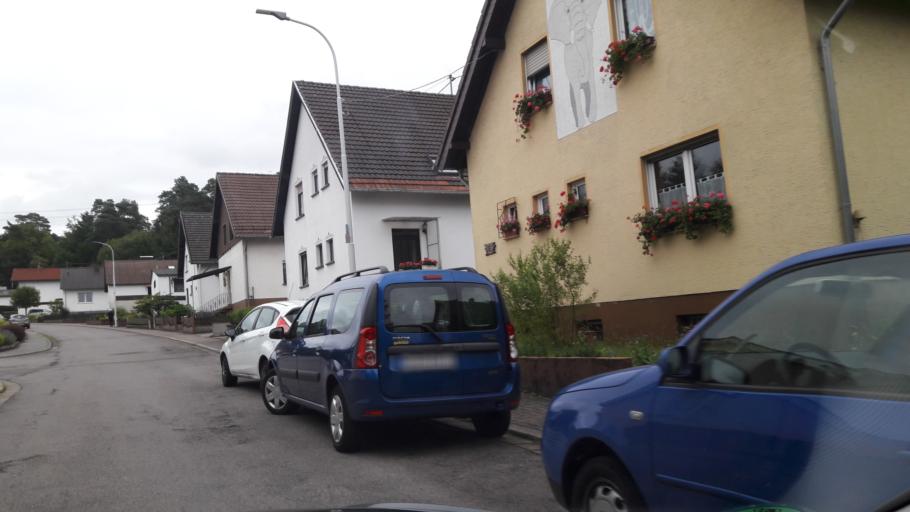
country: DE
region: Saarland
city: Bexbach
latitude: 49.3457
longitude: 7.2953
